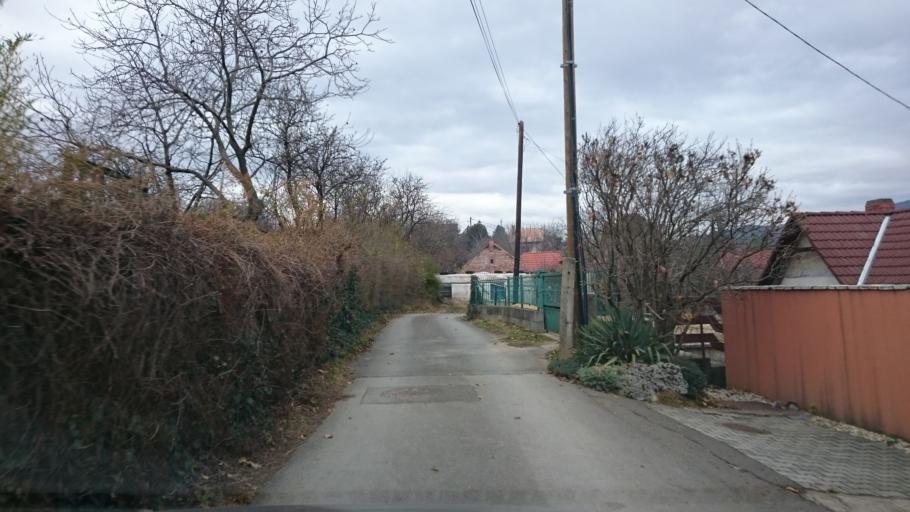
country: HU
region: Baranya
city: Pellerd
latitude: 46.0741
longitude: 18.1805
